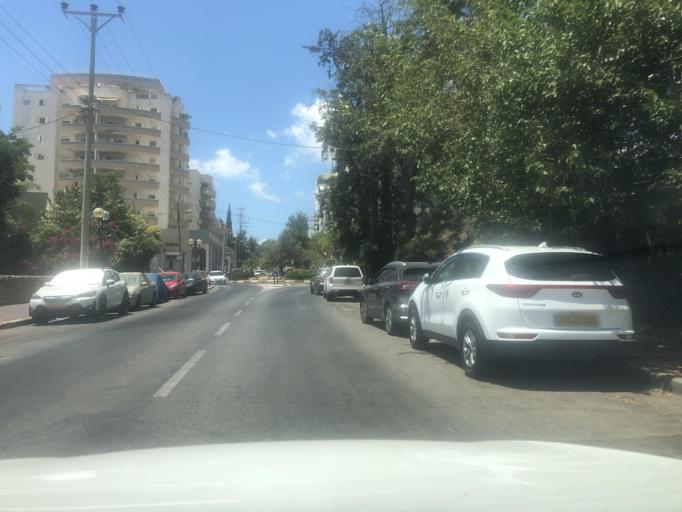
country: IL
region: Central District
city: Hod HaSharon
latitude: 32.1593
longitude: 34.9066
